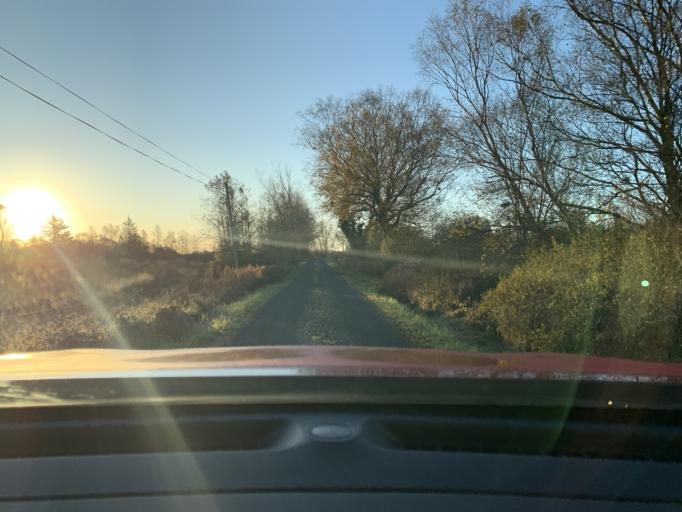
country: IE
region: Connaught
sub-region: Sligo
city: Ballymote
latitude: 54.0831
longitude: -8.5478
